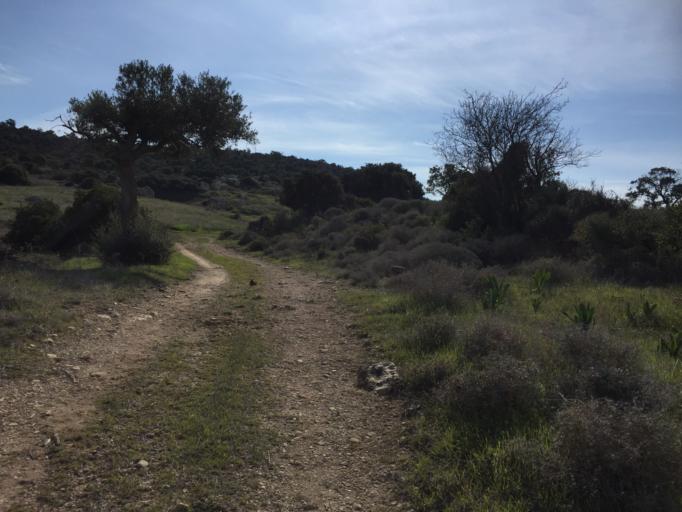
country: CY
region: Limassol
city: Mouttagiaka
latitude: 34.7449
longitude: 33.1145
